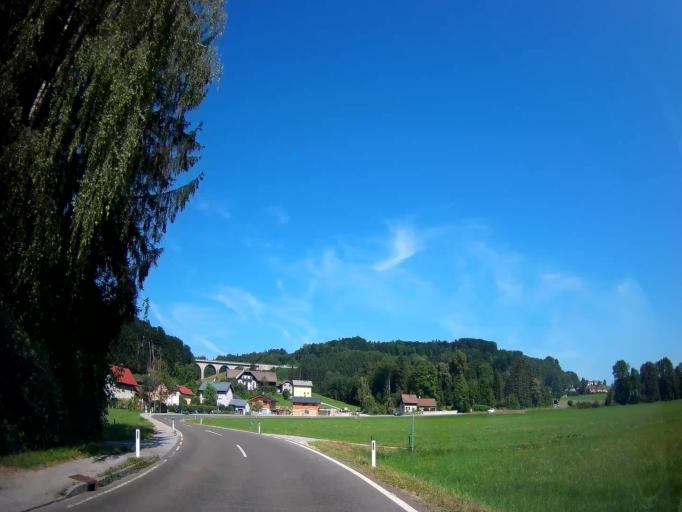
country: AT
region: Salzburg
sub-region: Politischer Bezirk Salzburg-Umgebung
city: Hallwang
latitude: 47.8338
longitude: 13.0818
